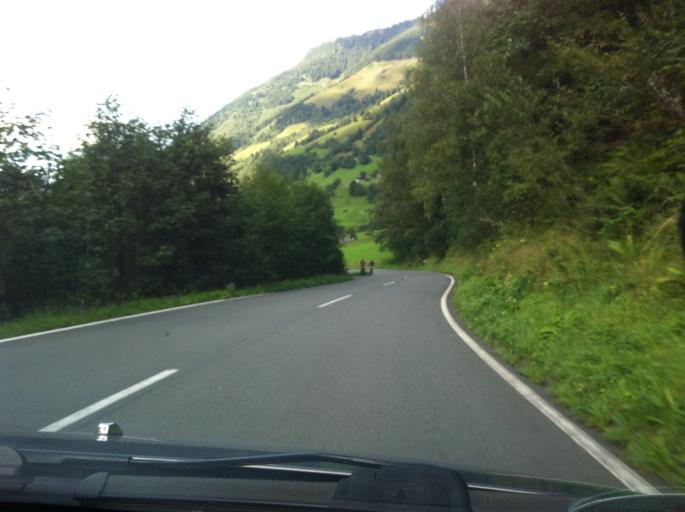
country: AT
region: Salzburg
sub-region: Politischer Bezirk Zell am See
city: Bruck an der Grossglocknerstrasse
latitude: 47.1972
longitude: 12.8338
